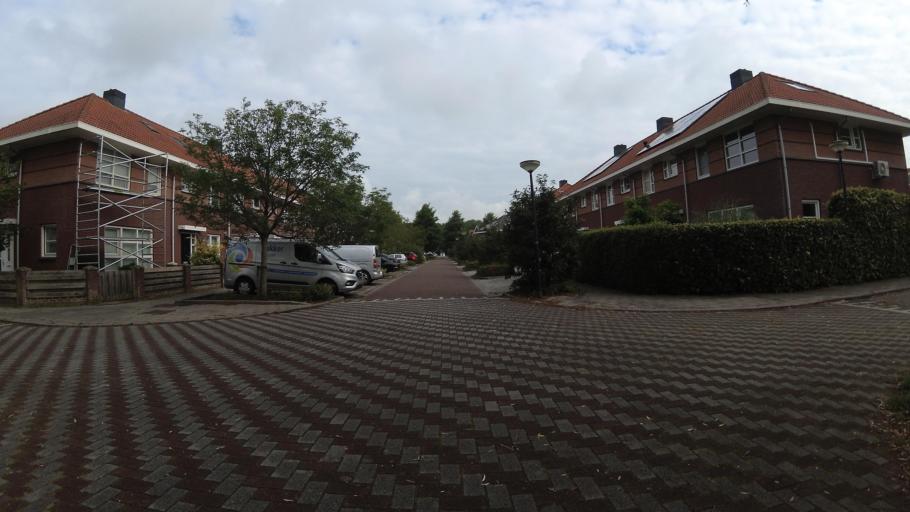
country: NL
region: North Holland
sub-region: Gemeente Schagen
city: Schagen
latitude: 52.8400
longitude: 4.8639
